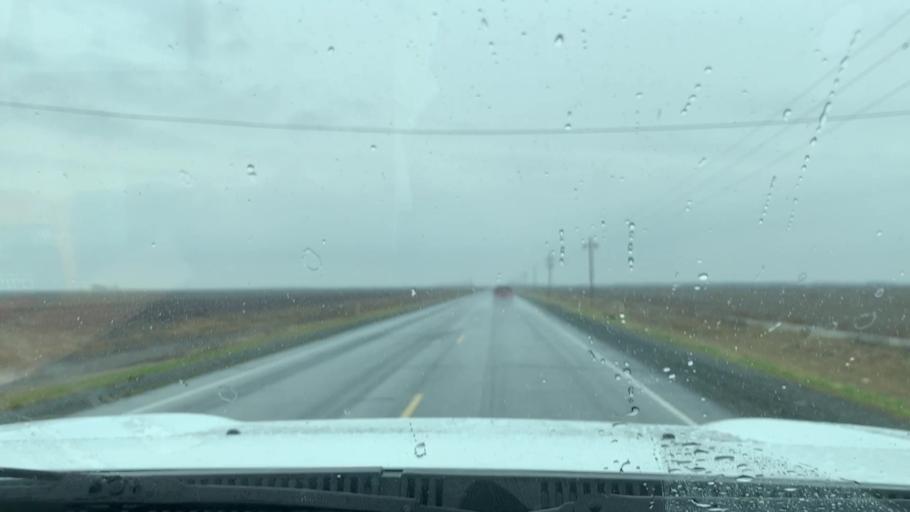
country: US
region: California
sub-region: Tulare County
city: Alpaugh
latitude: 35.9261
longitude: -119.4306
